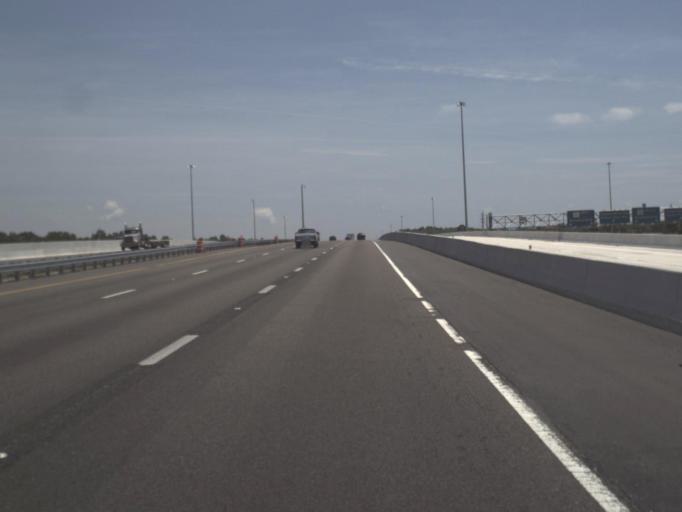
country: US
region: Florida
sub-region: Clay County
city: Bellair-Meadowbrook Terrace
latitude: 30.1977
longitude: -81.7425
